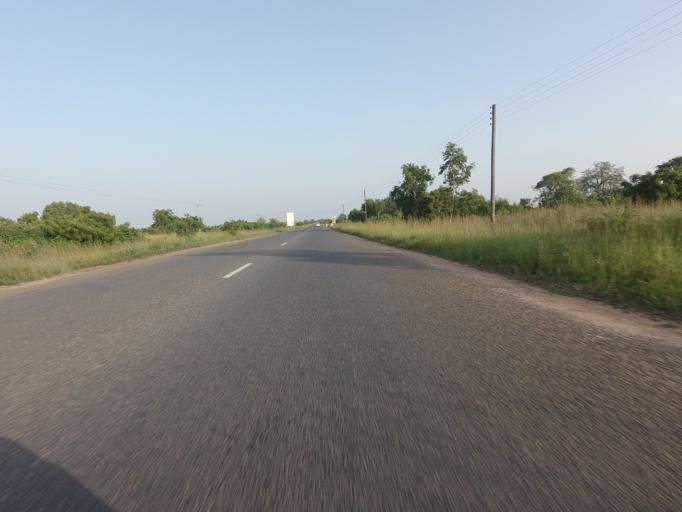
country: GH
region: Volta
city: Anloga
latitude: 6.0065
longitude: 0.6692
